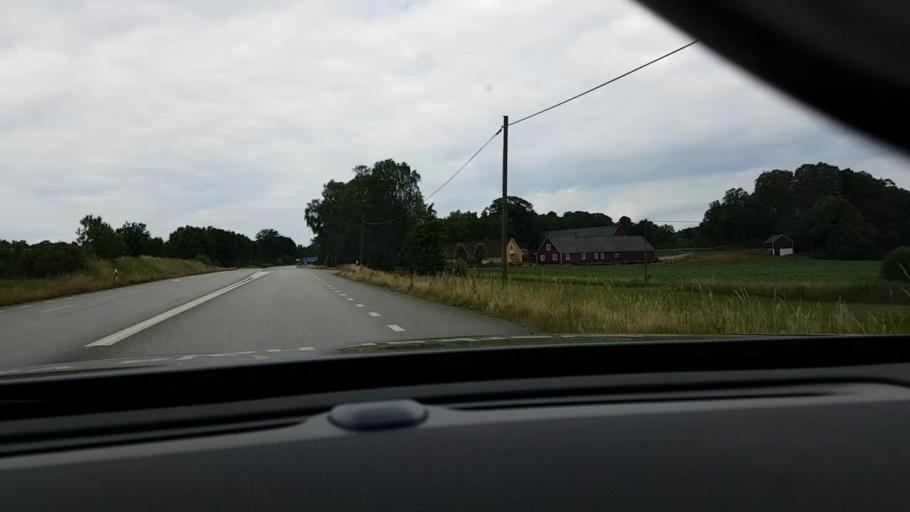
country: SE
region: Skane
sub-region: Hassleholms Kommun
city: Tormestorp
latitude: 56.0725
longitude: 13.7436
